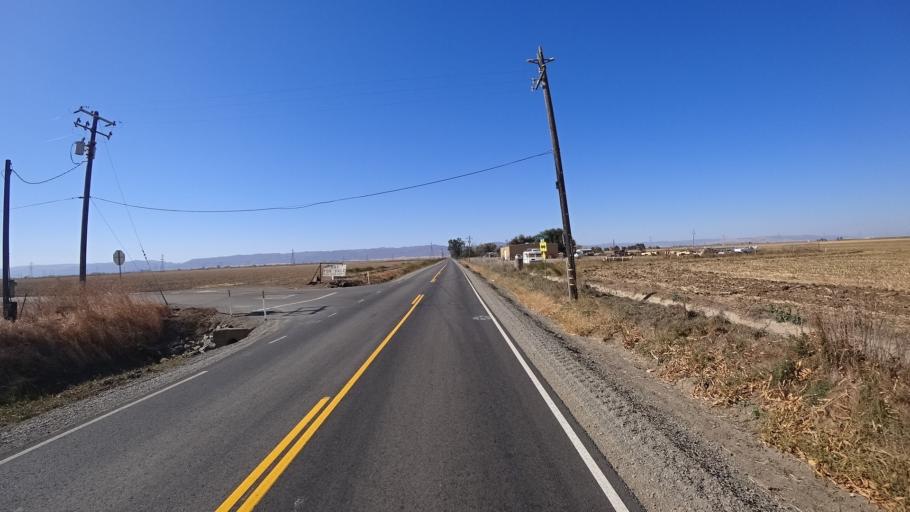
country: US
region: California
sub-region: Yolo County
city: Cottonwood
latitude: 38.6201
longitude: -121.9135
